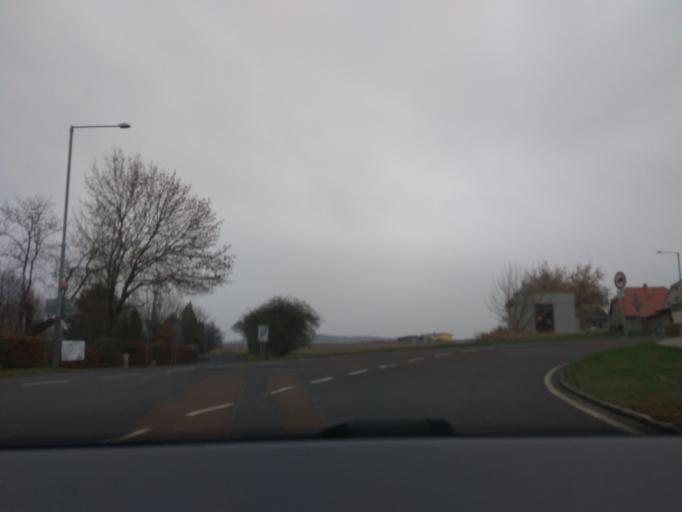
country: CZ
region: Central Bohemia
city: Hovorcovice
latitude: 50.1626
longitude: 14.5253
